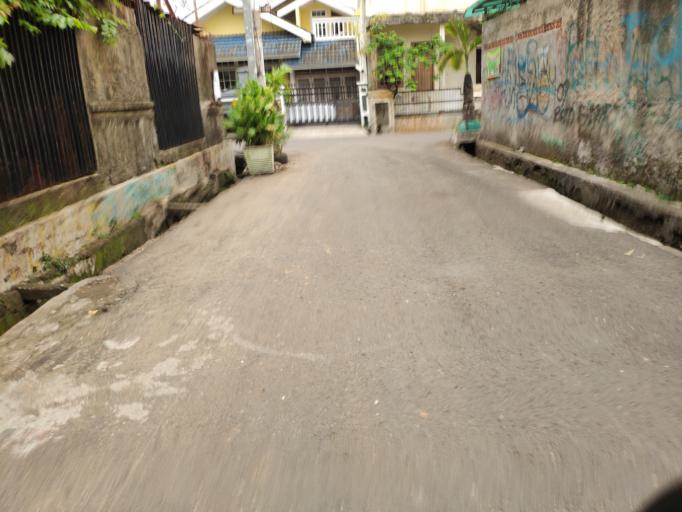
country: ID
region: Jakarta Raya
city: Jakarta
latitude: -6.1967
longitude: 106.8656
